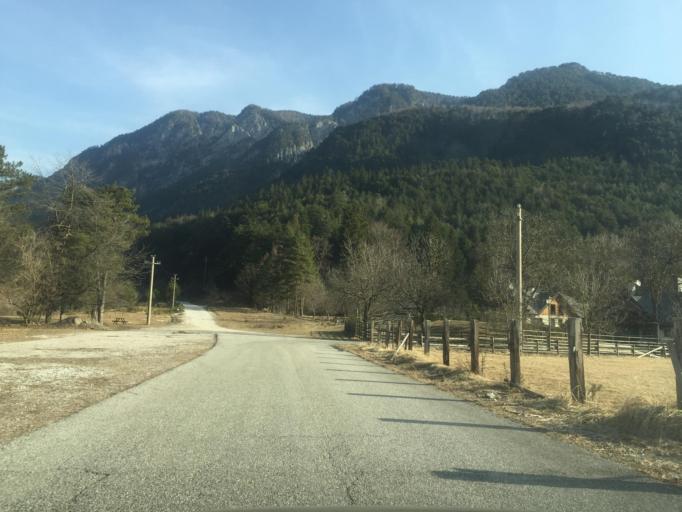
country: IT
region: Friuli Venezia Giulia
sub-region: Provincia di Udine
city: Malborghetto
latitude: 46.5026
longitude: 13.3963
